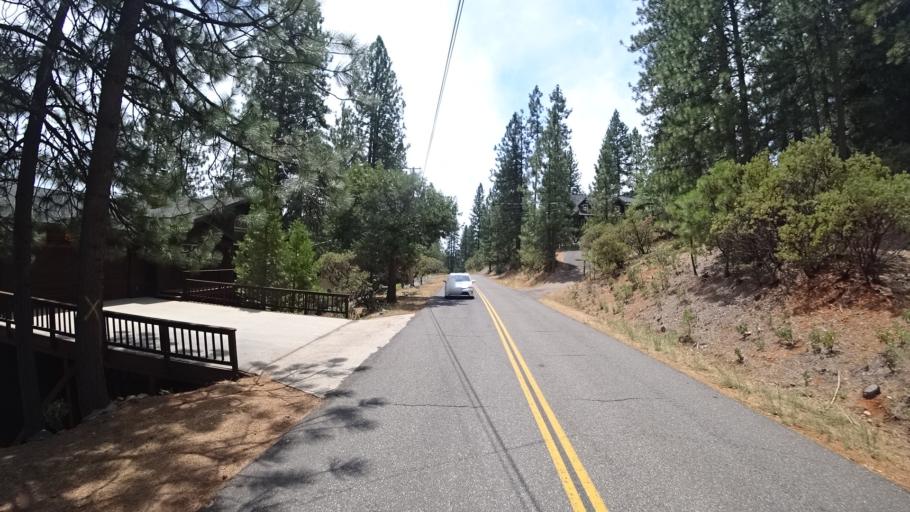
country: US
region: California
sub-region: Calaveras County
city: Arnold
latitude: 38.2415
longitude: -120.3523
